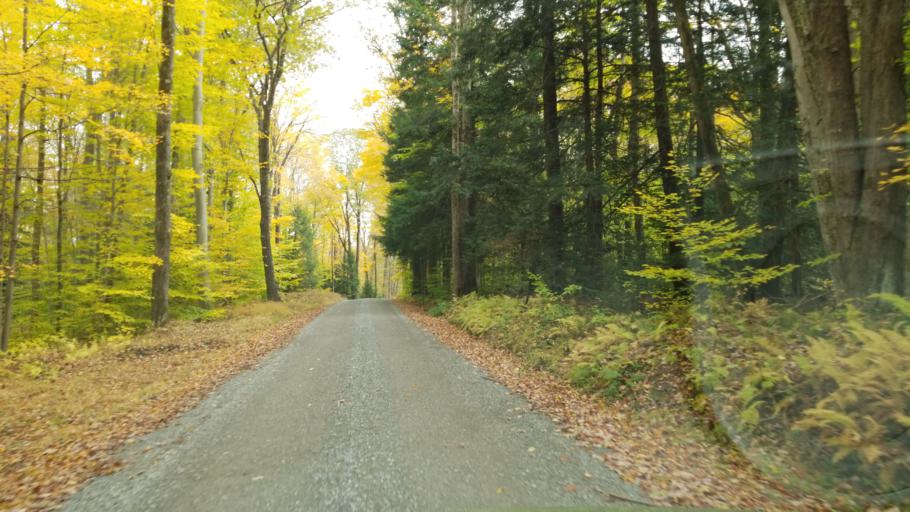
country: US
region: Pennsylvania
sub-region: Clearfield County
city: Clearfield
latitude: 41.1975
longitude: -78.4113
